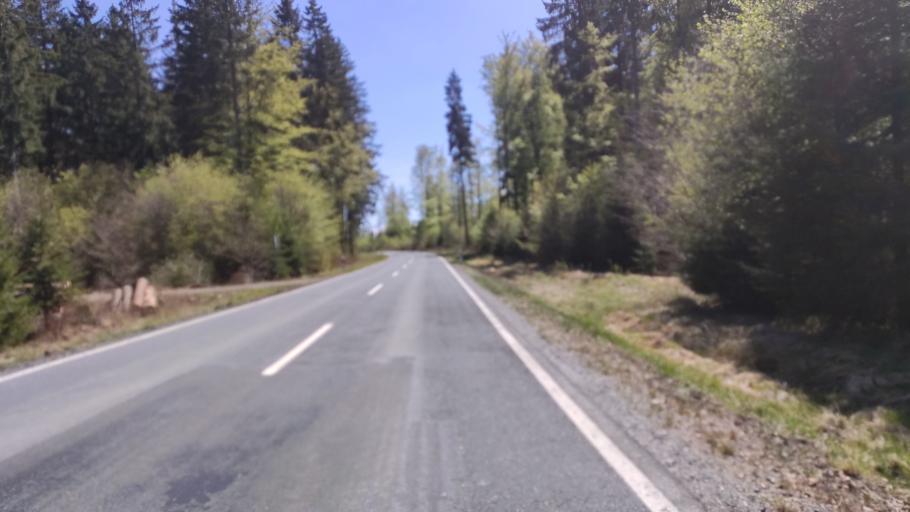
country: DE
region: Bavaria
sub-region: Upper Franconia
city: Tschirn
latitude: 50.3619
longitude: 11.4652
